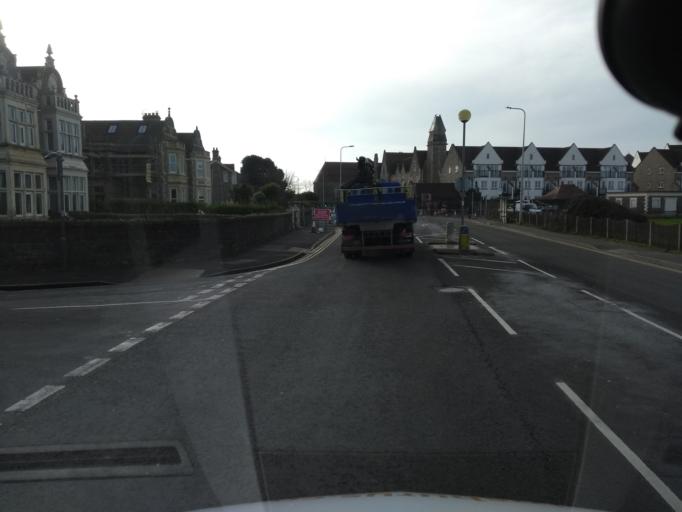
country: GB
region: England
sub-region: North Somerset
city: Weston-super-Mare
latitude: 51.3353
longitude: -2.9824
